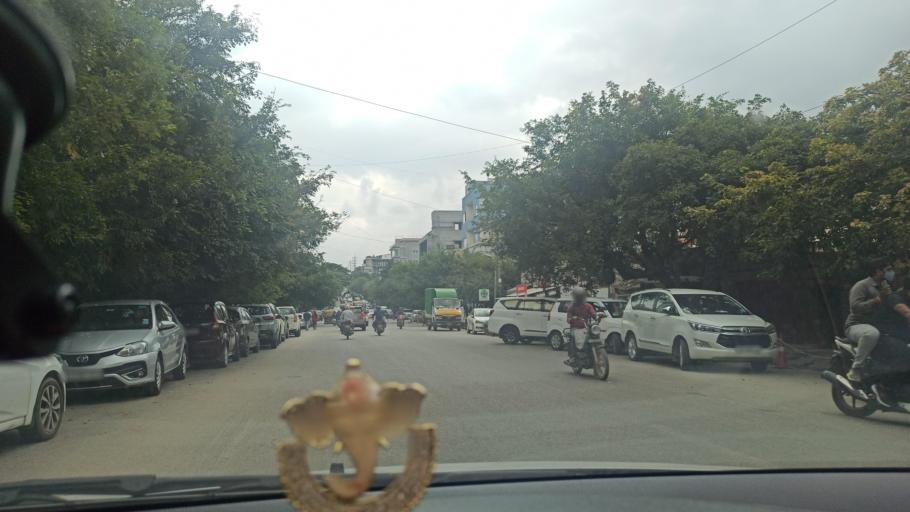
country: IN
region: Karnataka
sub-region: Bangalore Urban
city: Bangalore
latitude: 12.9166
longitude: 77.6449
